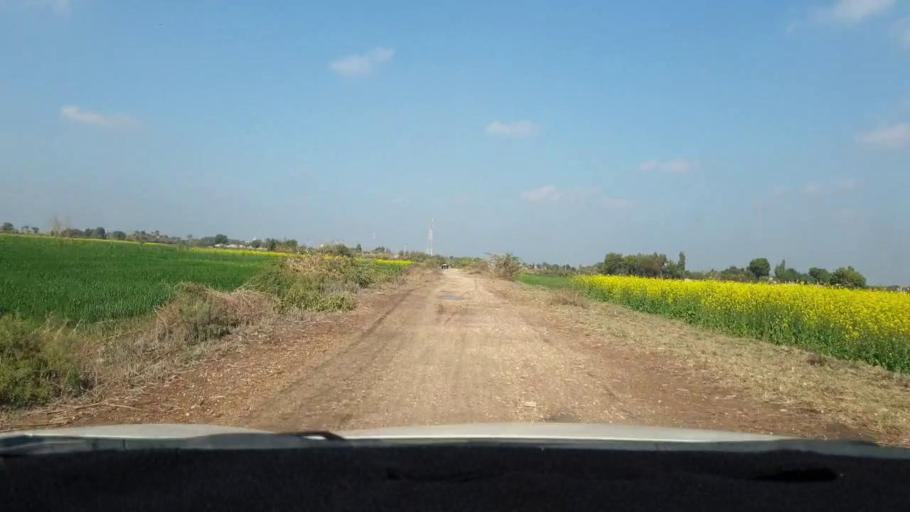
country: PK
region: Sindh
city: Berani
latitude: 25.7705
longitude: 68.8606
